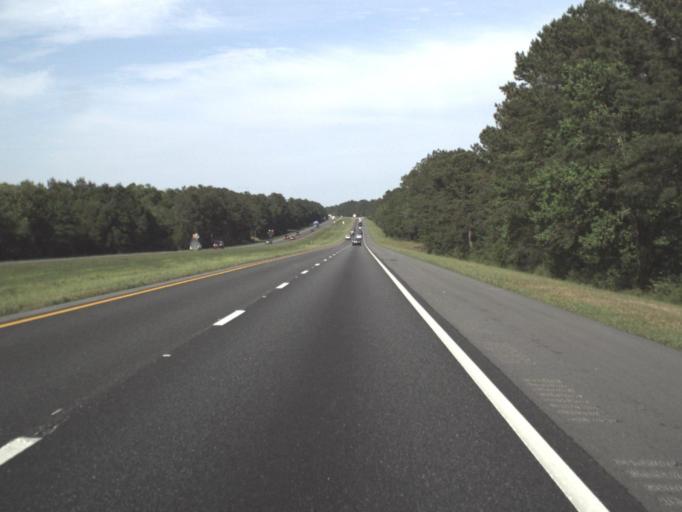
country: US
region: Florida
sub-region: Walton County
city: DeFuniak Springs
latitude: 30.7223
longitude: -85.9148
